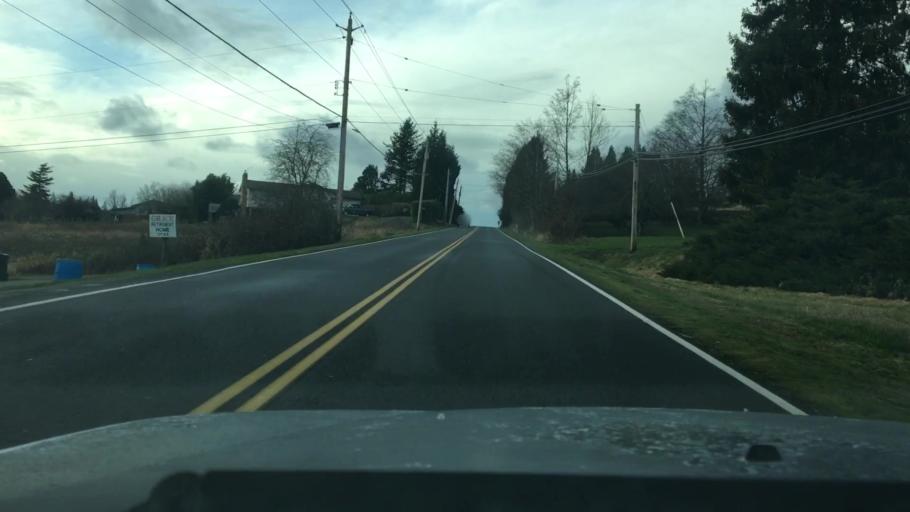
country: US
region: Washington
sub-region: Whatcom County
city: Ferndale
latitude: 48.8484
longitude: -122.6188
